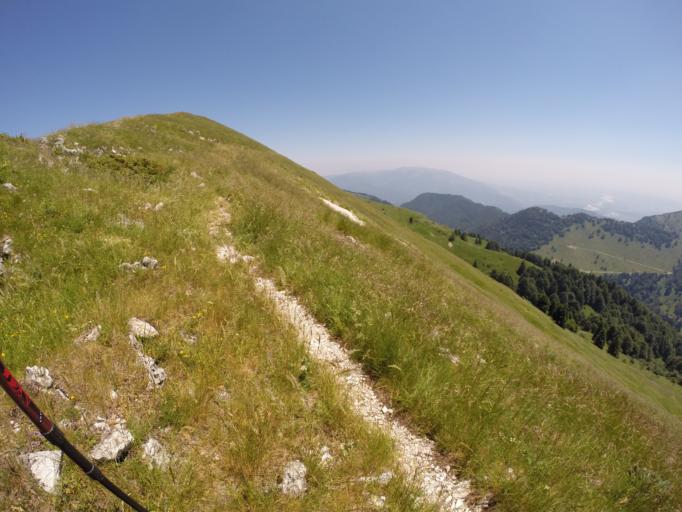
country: IT
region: Veneto
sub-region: Provincia di Treviso
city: Crespano del Grappa
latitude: 45.9062
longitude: 11.8235
